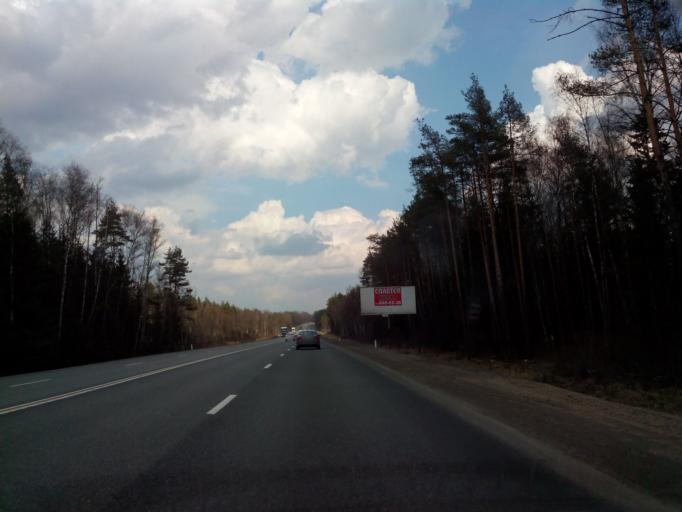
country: RU
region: Moskovskaya
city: Dorokhovo
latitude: 55.5452
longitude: 36.4349
